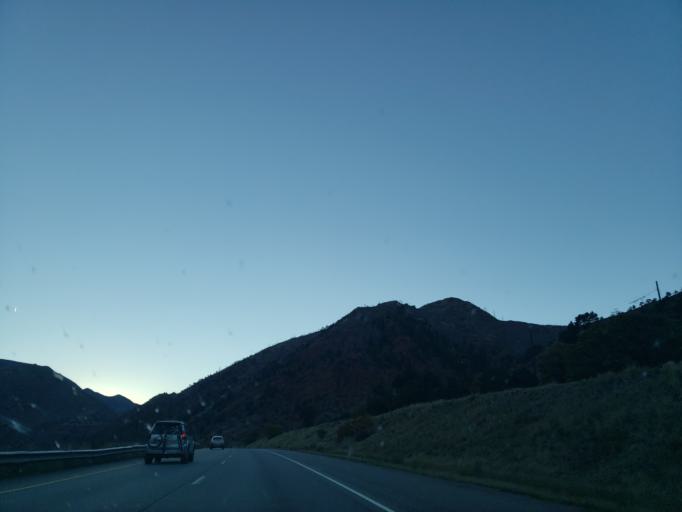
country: US
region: Colorado
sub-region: Garfield County
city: Glenwood Springs
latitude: 39.5612
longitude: -107.3825
